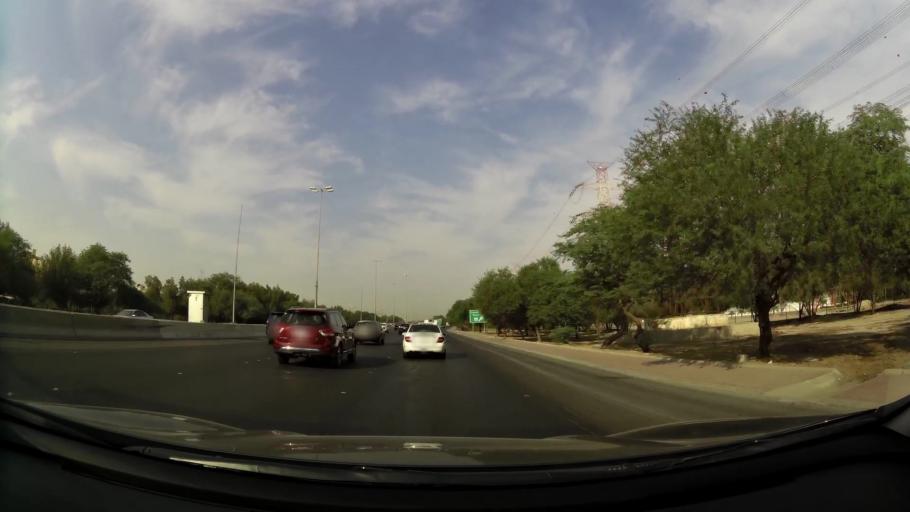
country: KW
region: Mubarak al Kabir
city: Sabah as Salim
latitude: 29.2646
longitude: 48.0508
